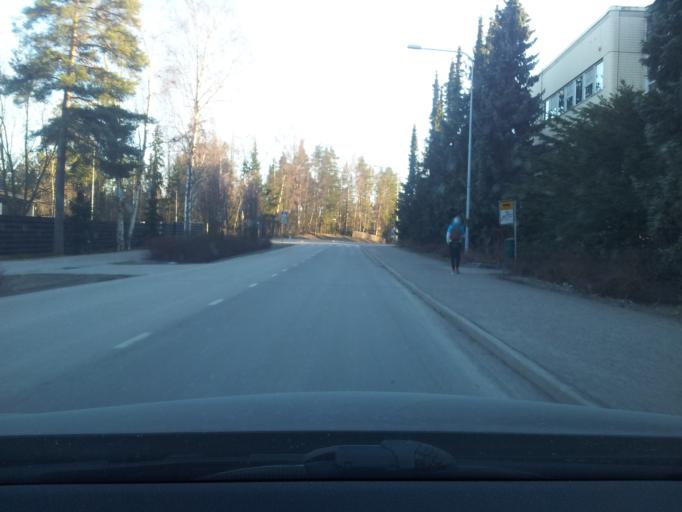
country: FI
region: Uusimaa
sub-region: Helsinki
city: Otaniemi
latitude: 60.1682
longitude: 24.8064
